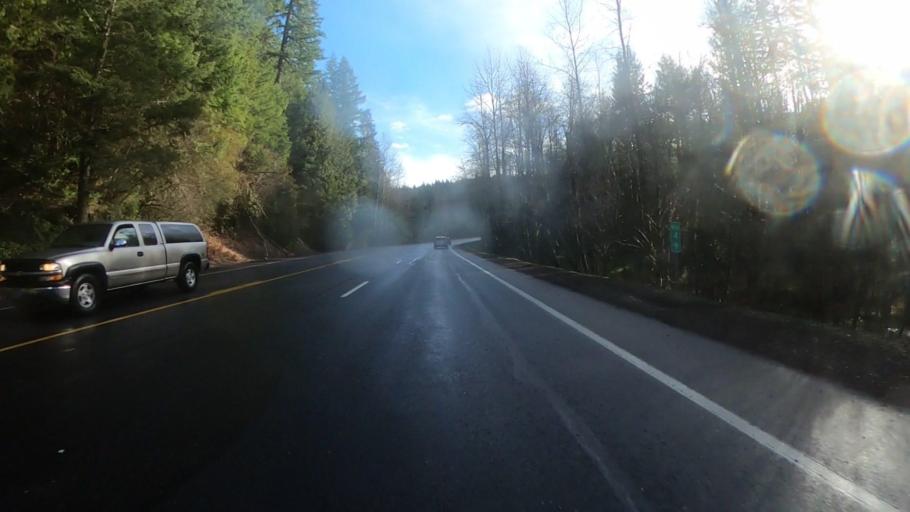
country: US
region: Oregon
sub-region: Lane County
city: Oakridge
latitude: 43.6707
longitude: -122.2353
